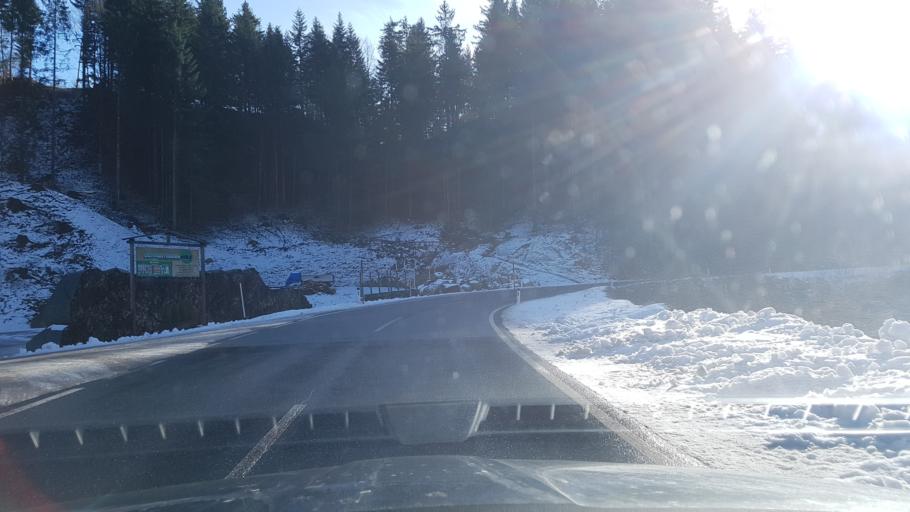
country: AT
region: Salzburg
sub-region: Politischer Bezirk Hallein
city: Krispl
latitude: 47.7175
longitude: 13.1921
